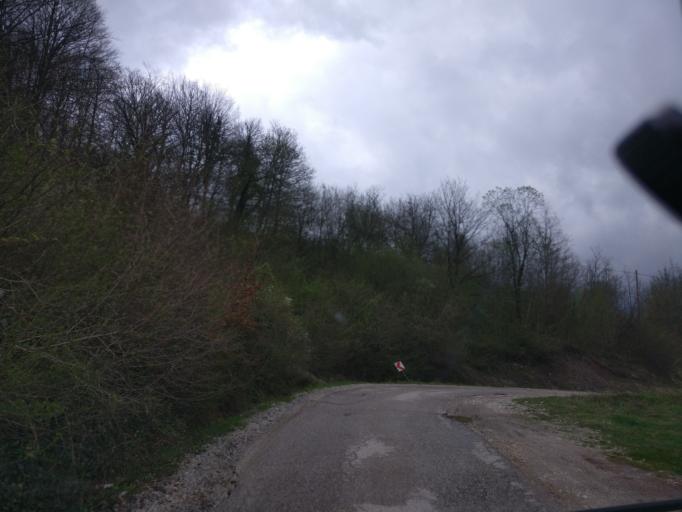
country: BA
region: Republika Srpska
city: Foca
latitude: 43.3530
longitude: 18.8264
